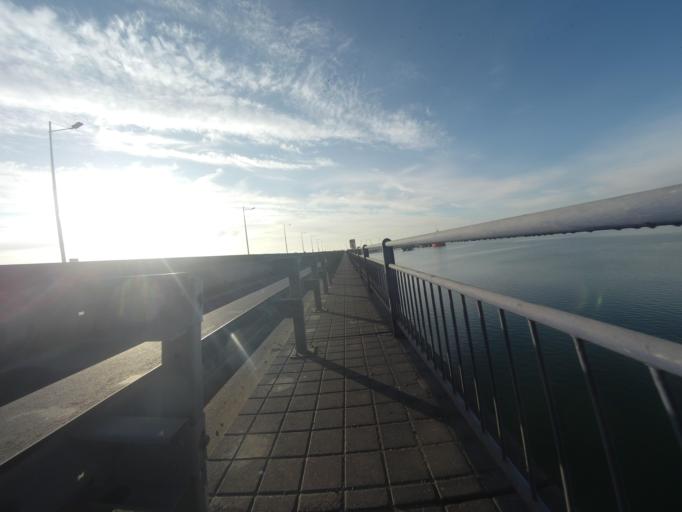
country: ES
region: Andalusia
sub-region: Provincia de Huelva
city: Punta Umbria
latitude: 37.2110
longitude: -6.9382
